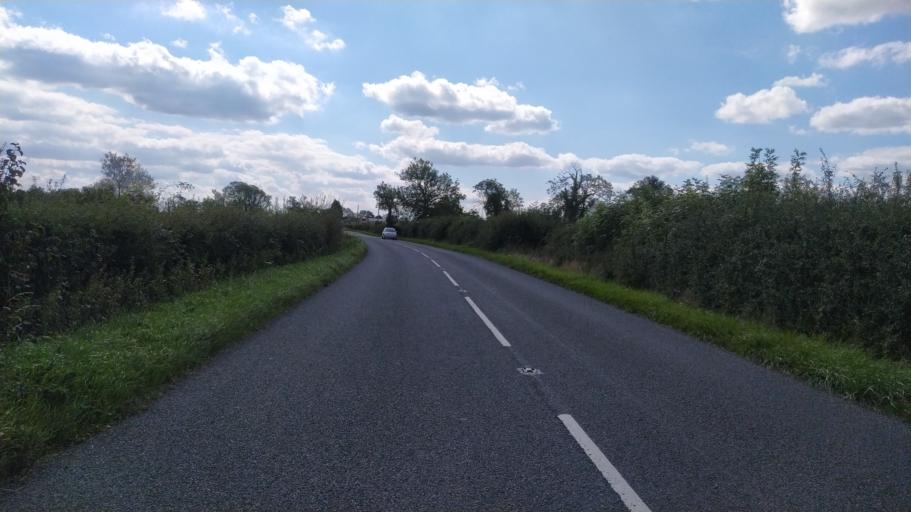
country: GB
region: England
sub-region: Wiltshire
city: Mere
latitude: 51.0808
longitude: -2.2808
